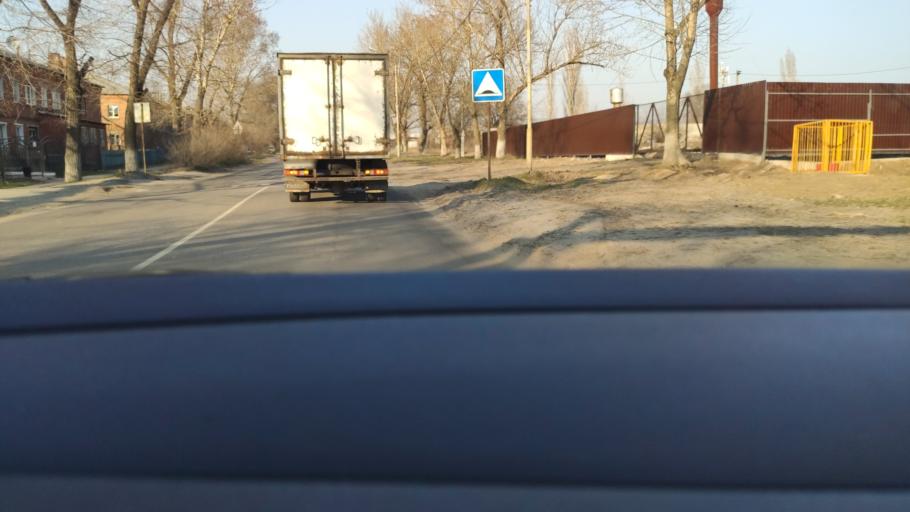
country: RU
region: Voronezj
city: Maslovka
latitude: 51.5816
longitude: 39.3166
